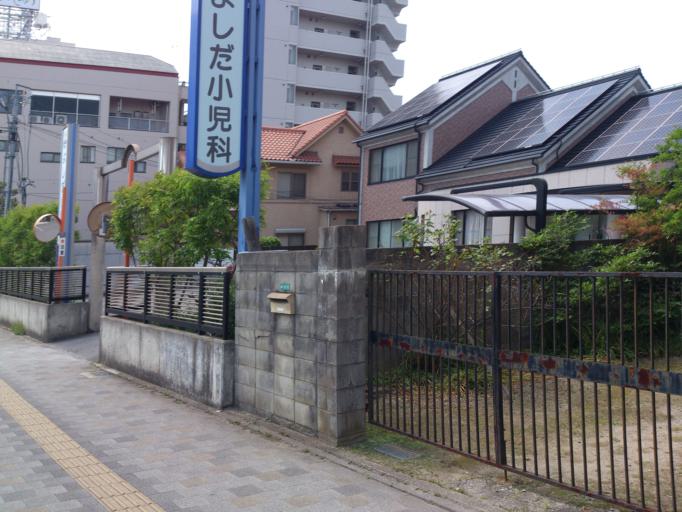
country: JP
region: Ehime
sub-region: Shikoku-chuo Shi
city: Matsuyama
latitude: 33.8475
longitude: 132.7764
